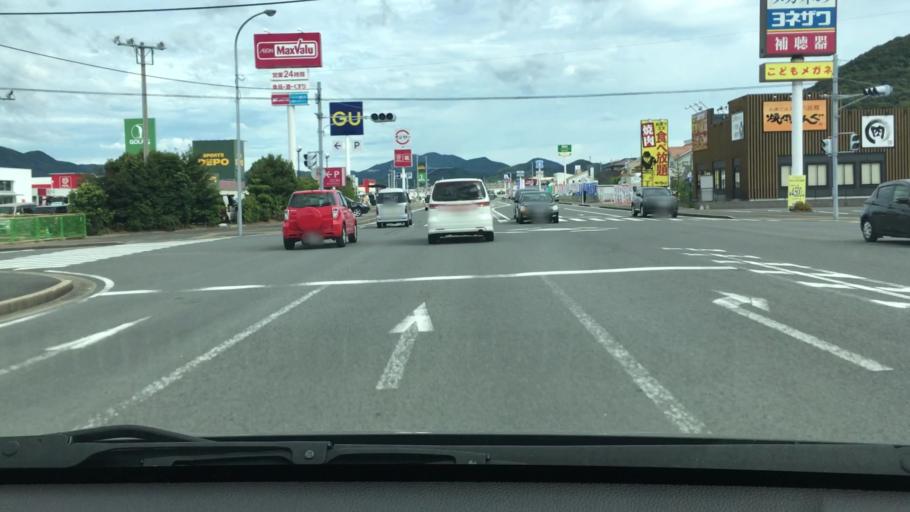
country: JP
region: Nagasaki
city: Togitsu
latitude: 32.8516
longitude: 129.8264
